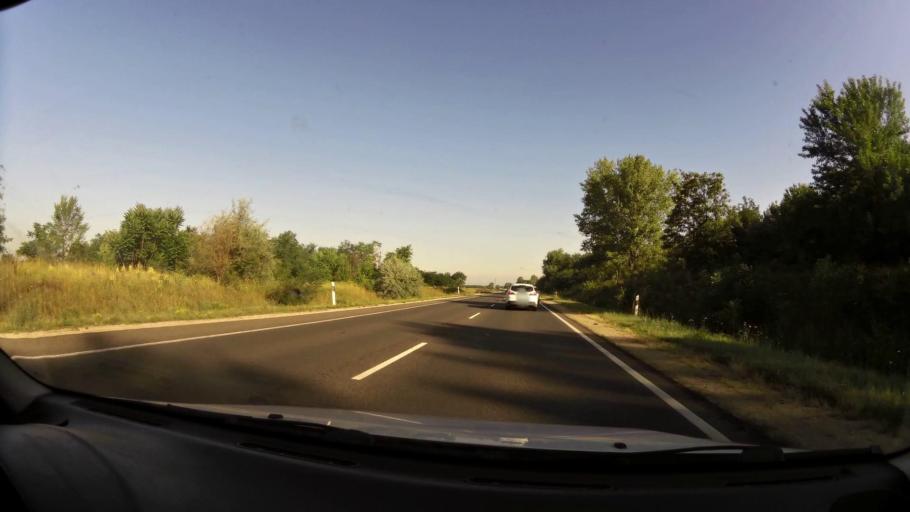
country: HU
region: Pest
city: Cegledbercel
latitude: 47.2462
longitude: 19.6503
